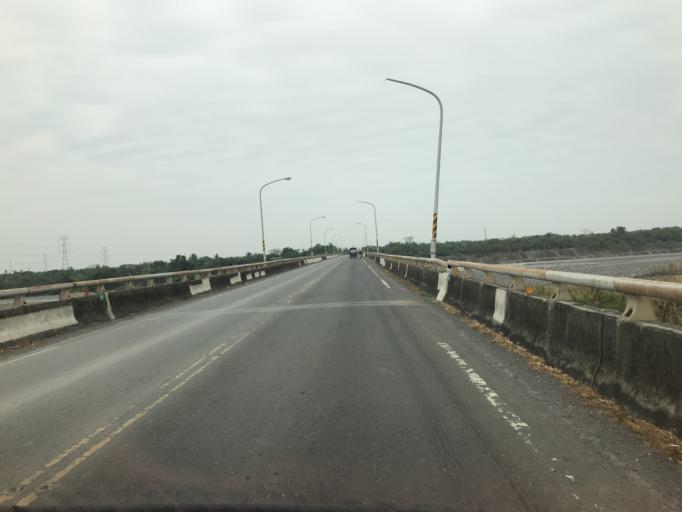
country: TW
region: Taiwan
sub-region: Pingtung
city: Pingtung
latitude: 22.4918
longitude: 120.5946
